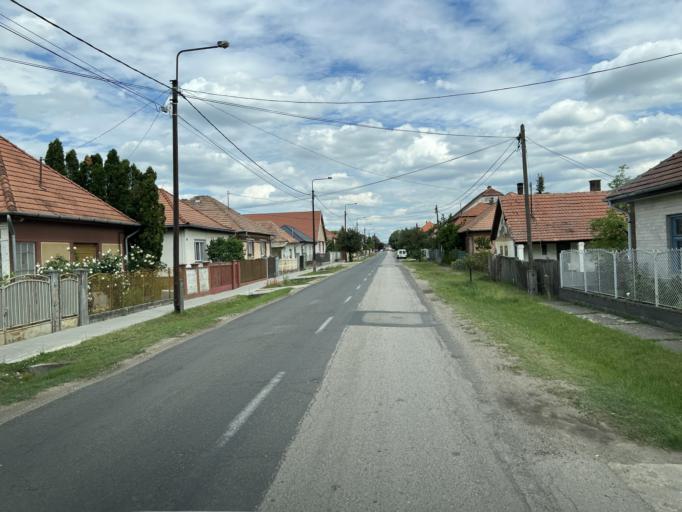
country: HU
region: Pest
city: Toalmas
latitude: 47.5067
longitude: 19.6617
